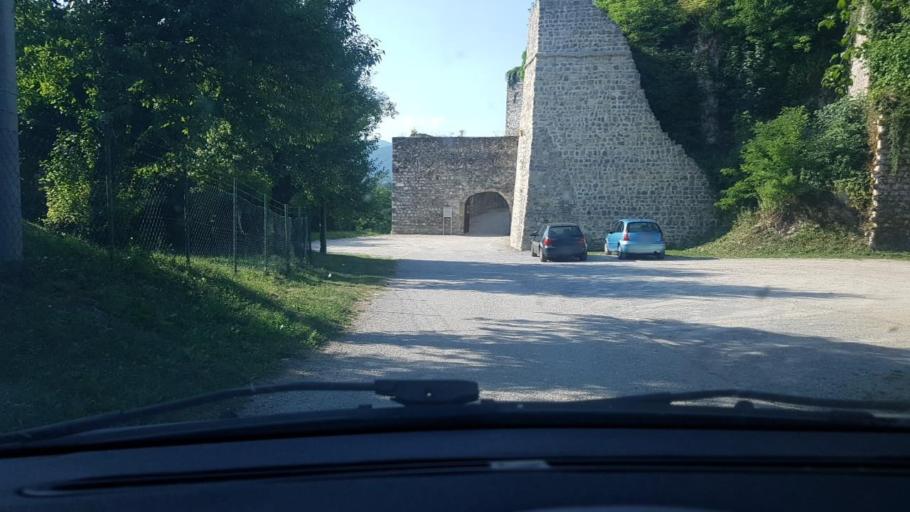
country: BA
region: Federation of Bosnia and Herzegovina
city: Ostrozac
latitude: 44.9065
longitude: 15.9374
